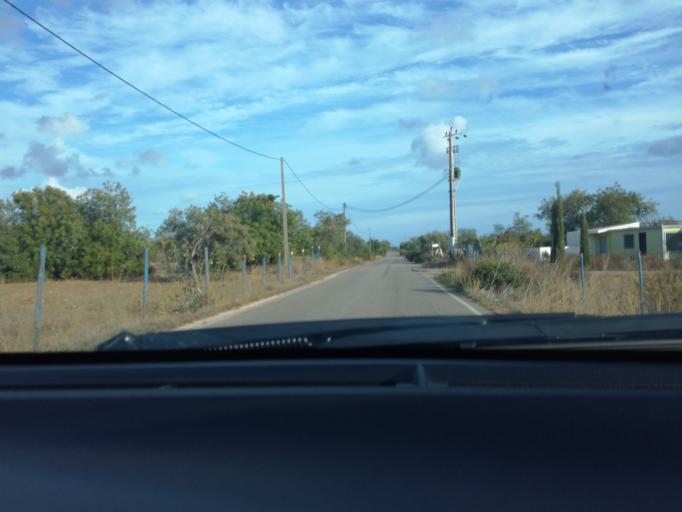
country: PT
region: Faro
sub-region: Olhao
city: Laranjeiro
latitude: 37.0798
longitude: -7.8316
